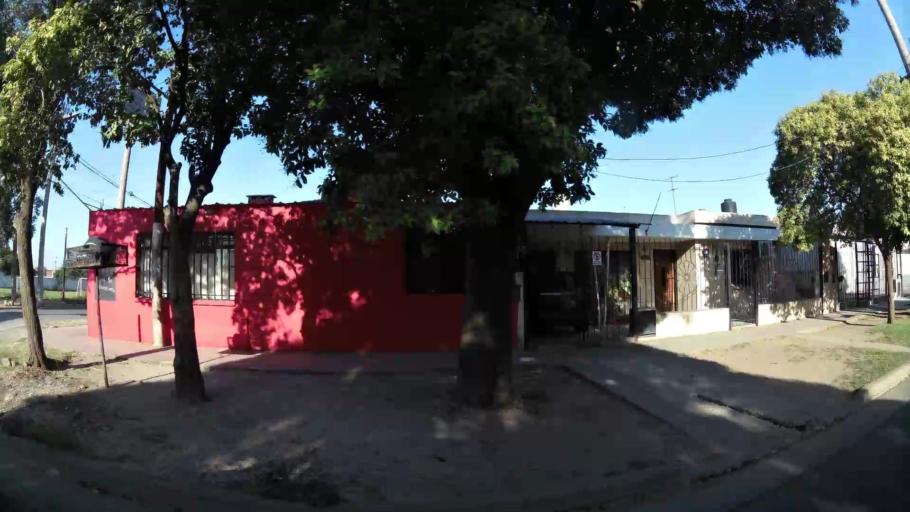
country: AR
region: Cordoba
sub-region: Departamento de Capital
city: Cordoba
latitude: -31.4445
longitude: -64.2481
